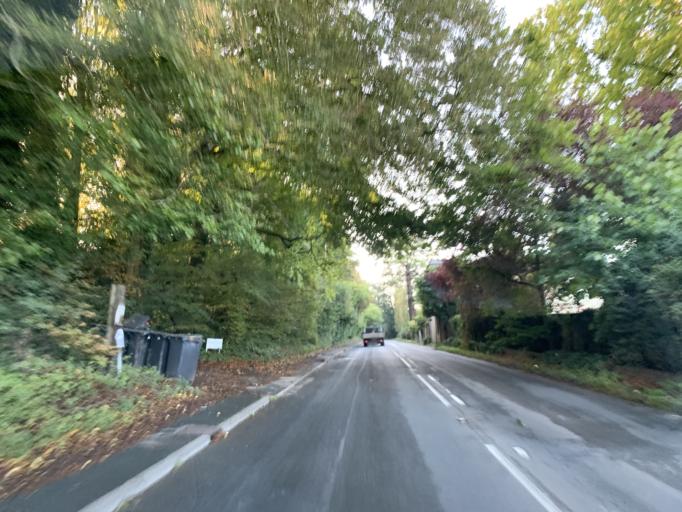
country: GB
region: England
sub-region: Wiltshire
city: Alderbury
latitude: 51.0556
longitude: -1.7574
